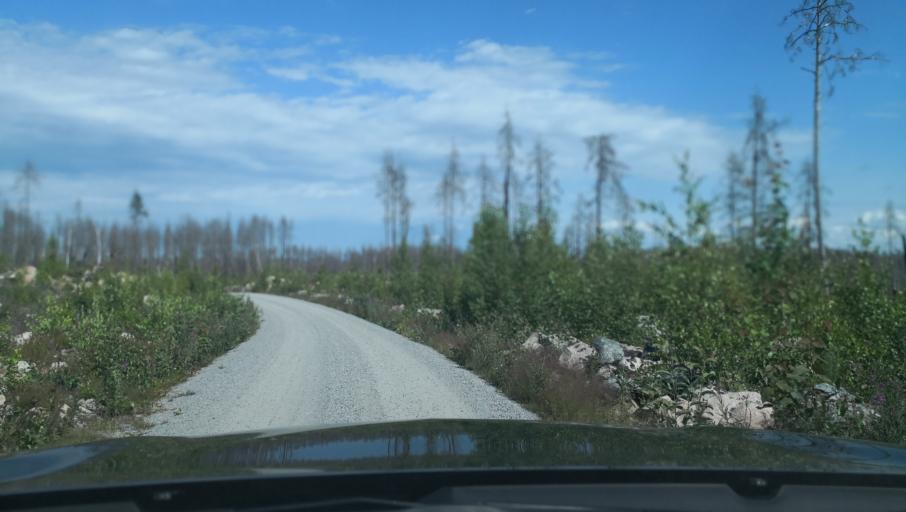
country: SE
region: Vaestmanland
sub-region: Surahammars Kommun
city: Ramnas
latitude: 59.9297
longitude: 16.1810
